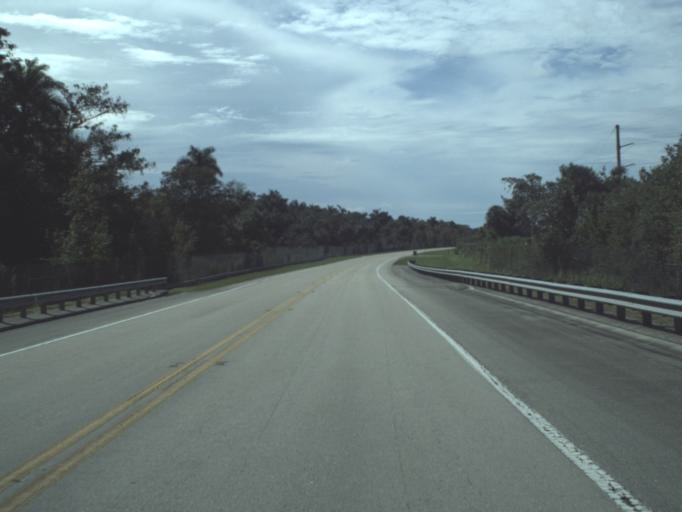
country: US
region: Florida
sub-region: Collier County
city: Orangetree
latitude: 26.0442
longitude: -81.3447
